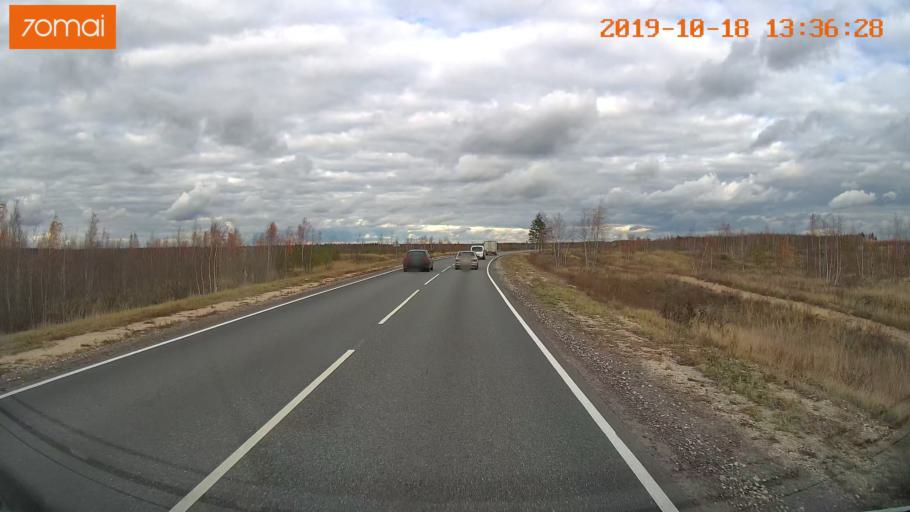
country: RU
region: Rjazan
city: Solotcha
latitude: 54.8705
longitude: 39.9850
